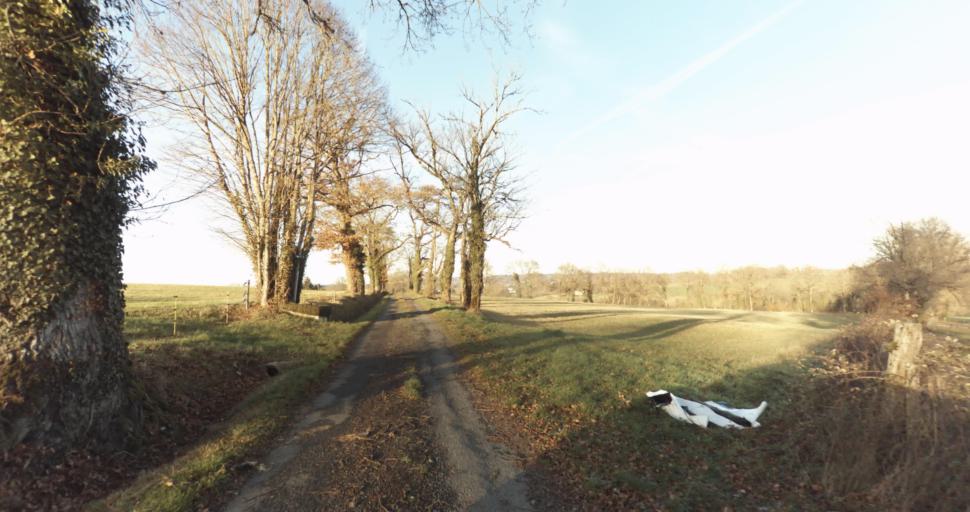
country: FR
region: Limousin
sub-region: Departement de la Haute-Vienne
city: Aixe-sur-Vienne
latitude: 45.7802
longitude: 1.1458
